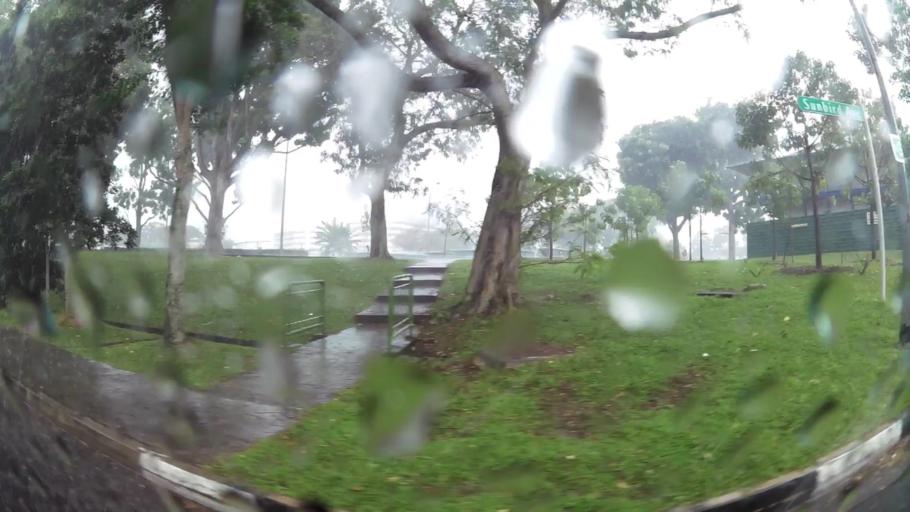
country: SG
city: Singapore
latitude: 1.3386
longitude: 103.9595
